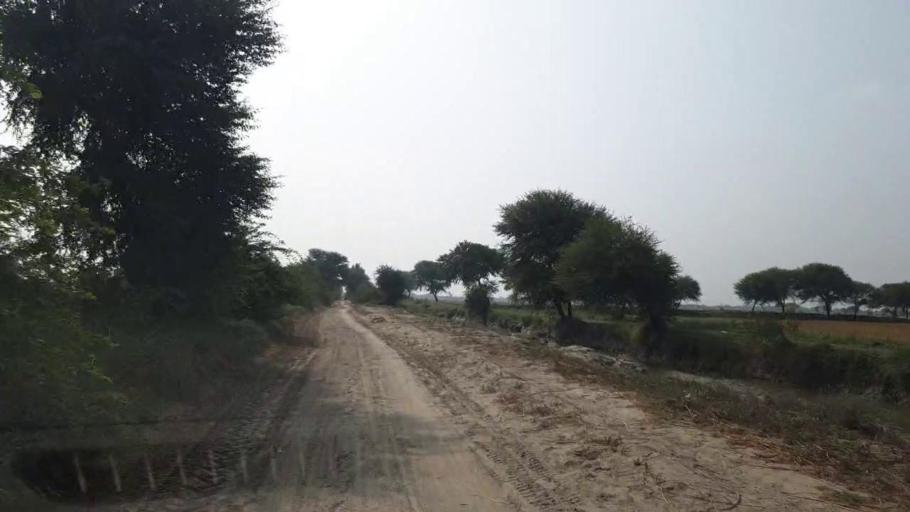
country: PK
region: Sindh
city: Kario
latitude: 24.7672
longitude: 68.5637
